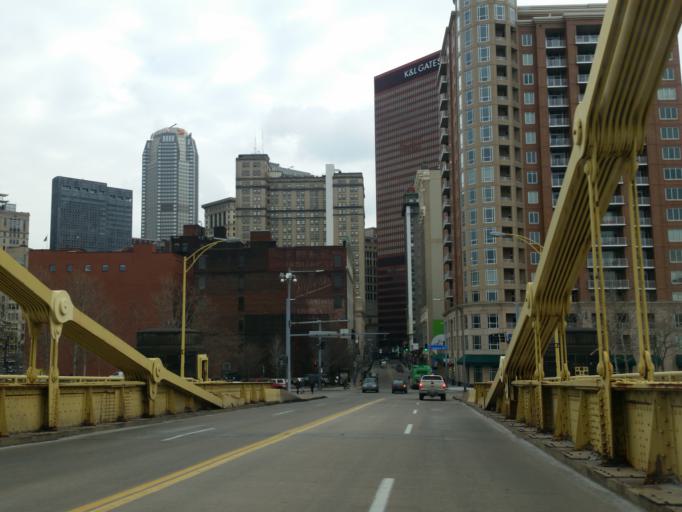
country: US
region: Pennsylvania
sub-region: Allegheny County
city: Pittsburgh
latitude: 40.4455
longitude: -80.0013
